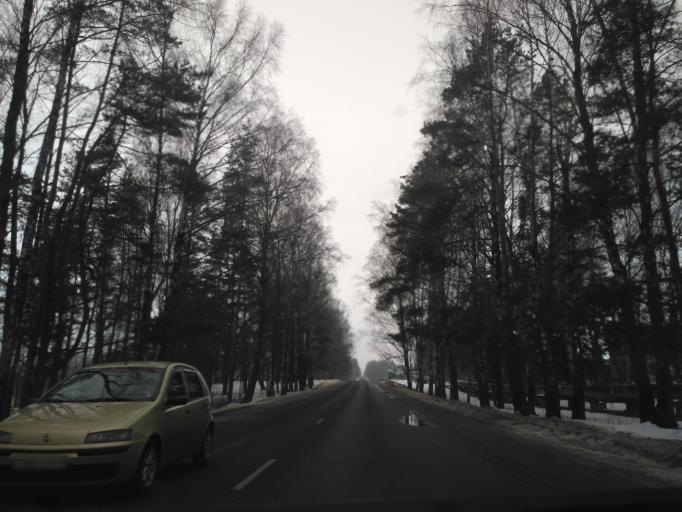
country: BY
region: Minsk
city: Horad Zhodzina
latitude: 54.0846
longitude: 28.3178
